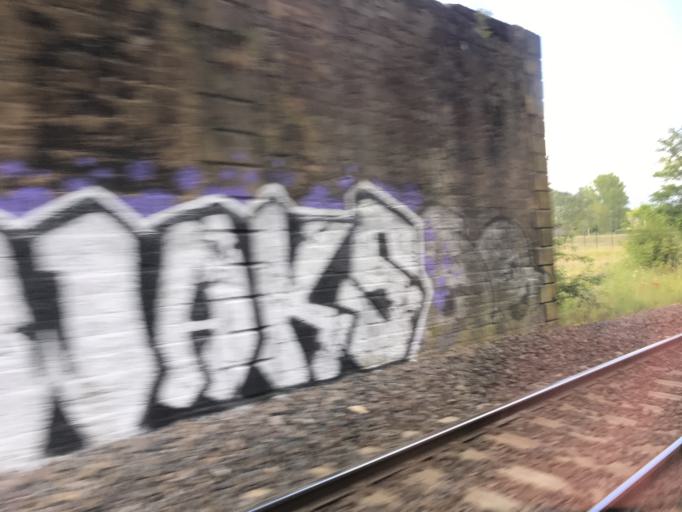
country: FR
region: Lorraine
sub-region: Departement de Meurthe-et-Moselle
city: Longwy
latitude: 49.5213
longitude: 5.7745
